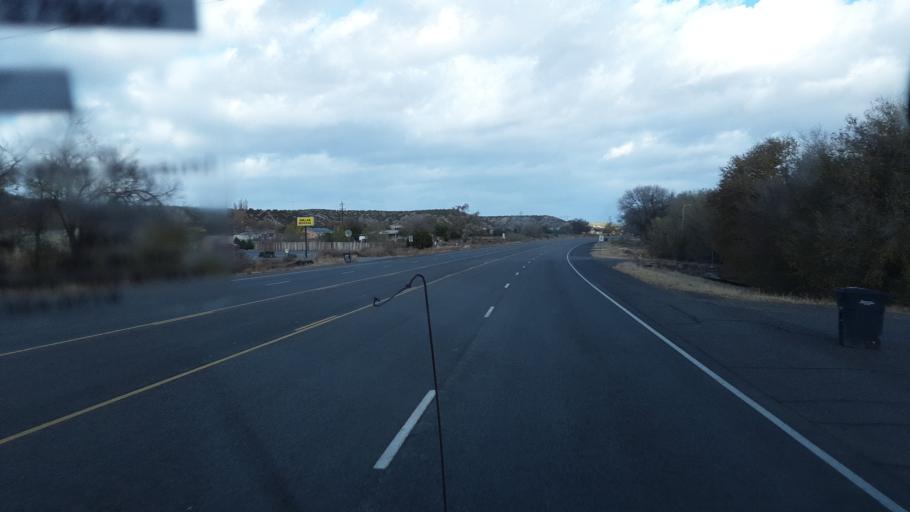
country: US
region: New Mexico
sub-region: Rio Arriba County
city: Ohkay Owingeh
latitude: 36.0483
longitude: -106.1103
